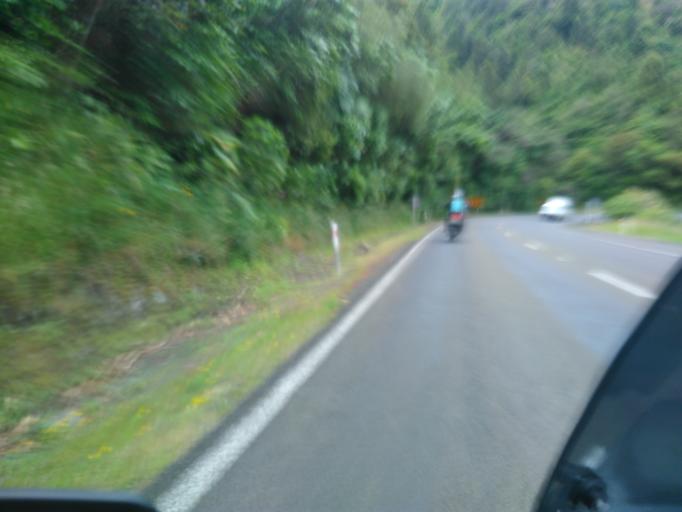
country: NZ
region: Bay of Plenty
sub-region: Opotiki District
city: Opotiki
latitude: -38.3022
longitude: 177.3946
